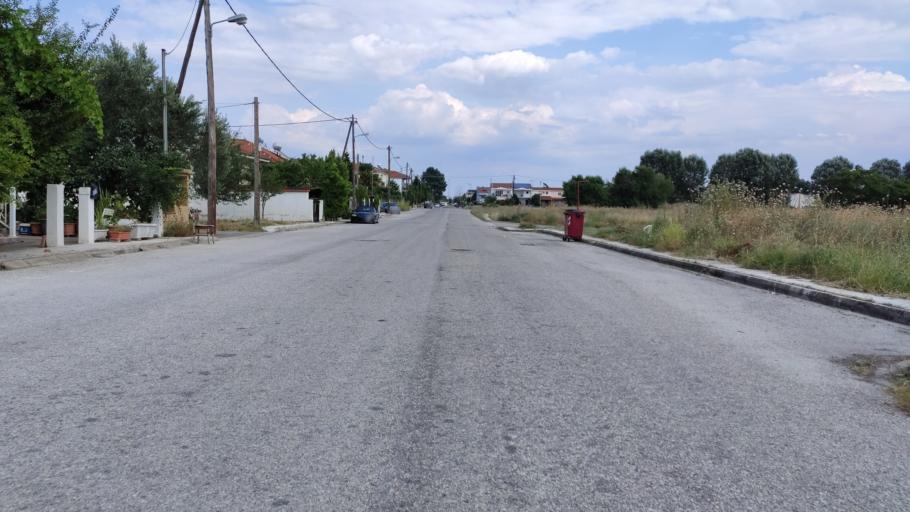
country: GR
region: East Macedonia and Thrace
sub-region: Nomos Rodopis
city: Komotini
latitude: 41.1298
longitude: 25.3933
